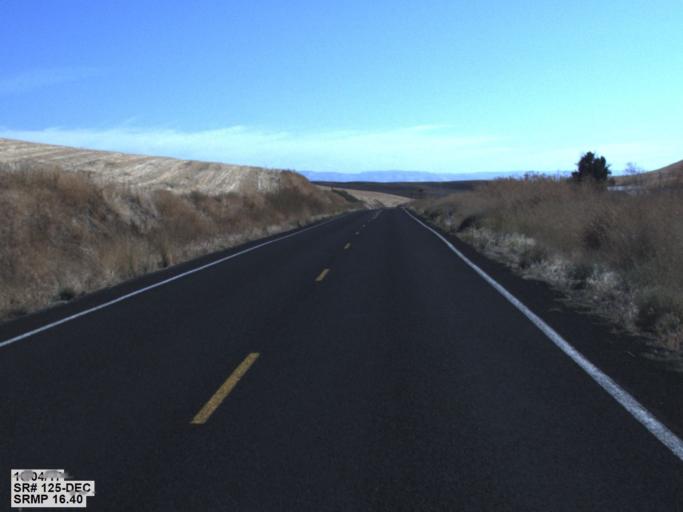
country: US
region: Washington
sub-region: Walla Walla County
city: Walla Walla
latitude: 46.2052
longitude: -118.3863
